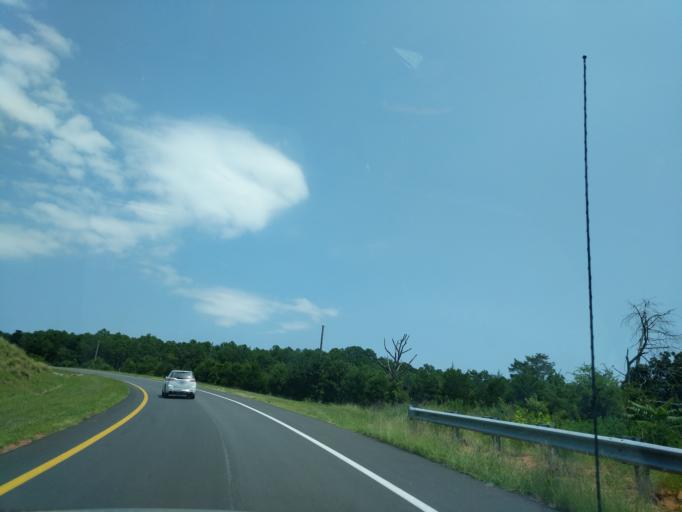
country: US
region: South Carolina
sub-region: Greenville County
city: Greer
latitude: 34.8746
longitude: -82.2151
